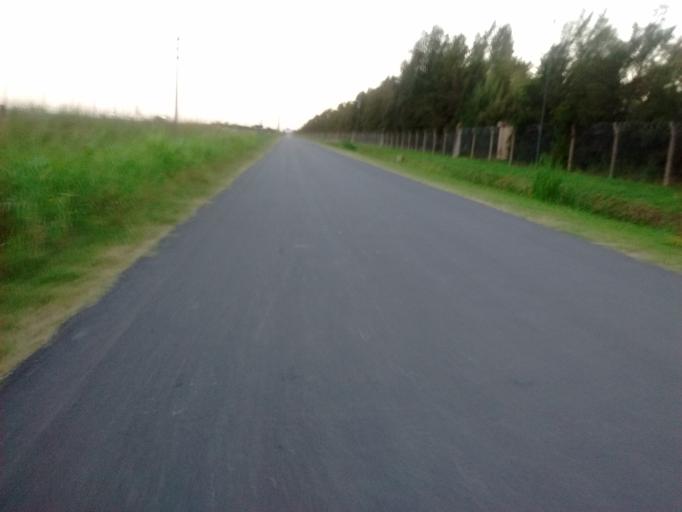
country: AR
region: Santa Fe
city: Funes
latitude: -32.9479
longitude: -60.8196
